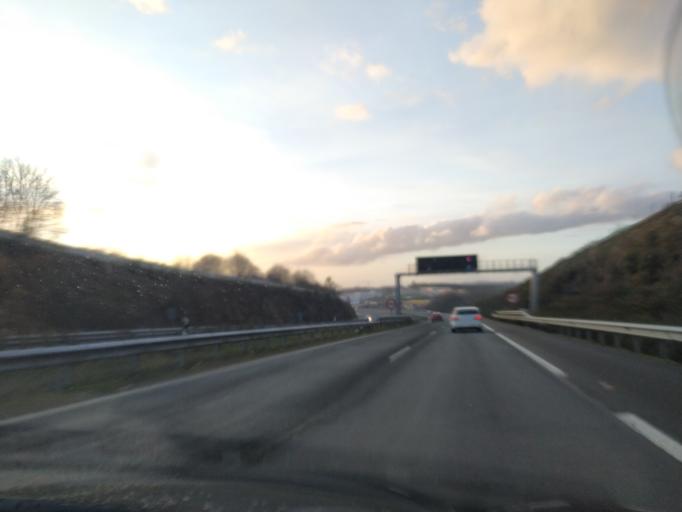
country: ES
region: Galicia
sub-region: Provincia da Coruna
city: Santiago de Compostela
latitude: 42.8995
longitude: -8.4890
